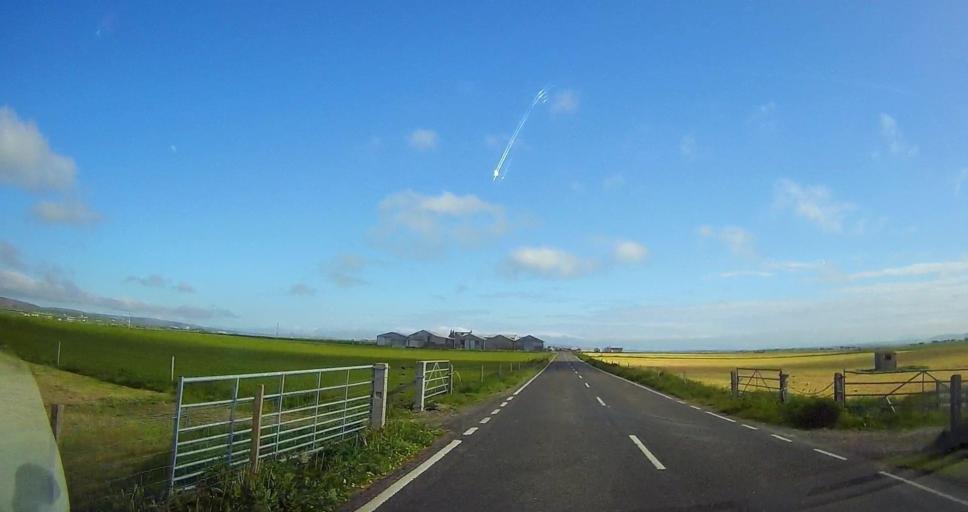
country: GB
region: Scotland
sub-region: Orkney Islands
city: Stromness
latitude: 59.0849
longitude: -3.2553
